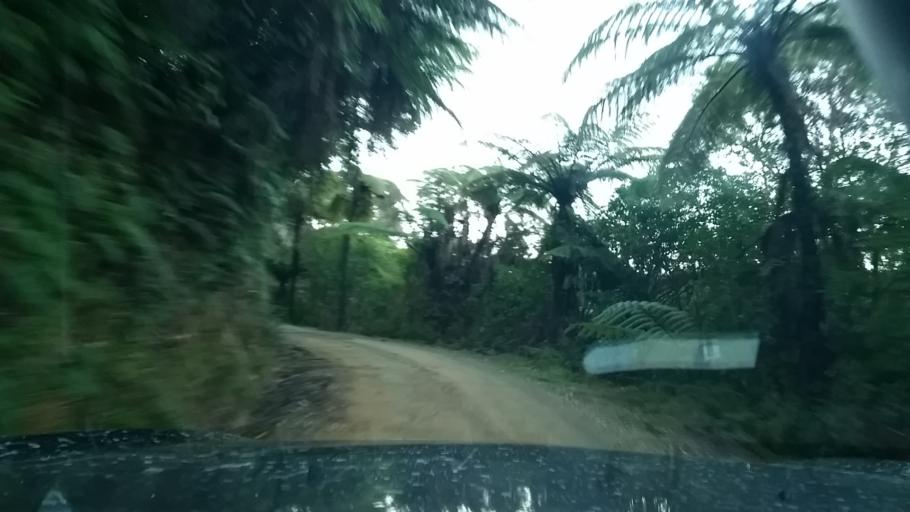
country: NZ
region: Marlborough
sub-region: Marlborough District
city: Picton
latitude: -41.1302
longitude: 174.1434
